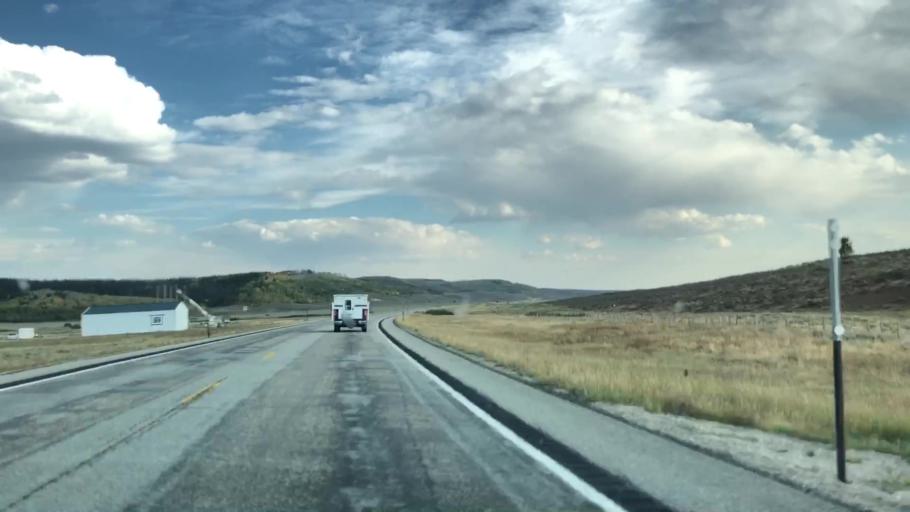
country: US
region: Wyoming
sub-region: Sublette County
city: Pinedale
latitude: 43.1165
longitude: -110.1775
